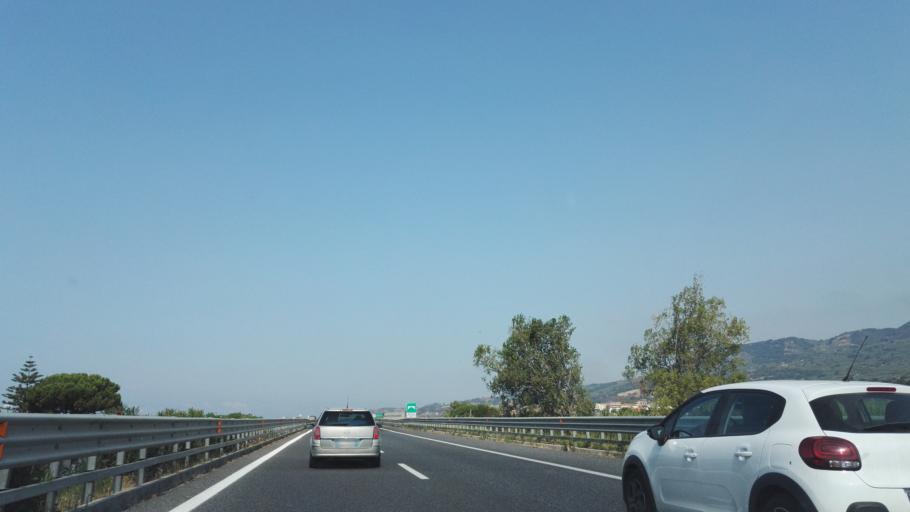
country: IT
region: Calabria
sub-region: Provincia di Catanzaro
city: Santa Eufemia Lamezia
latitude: 38.9330
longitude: 16.2235
